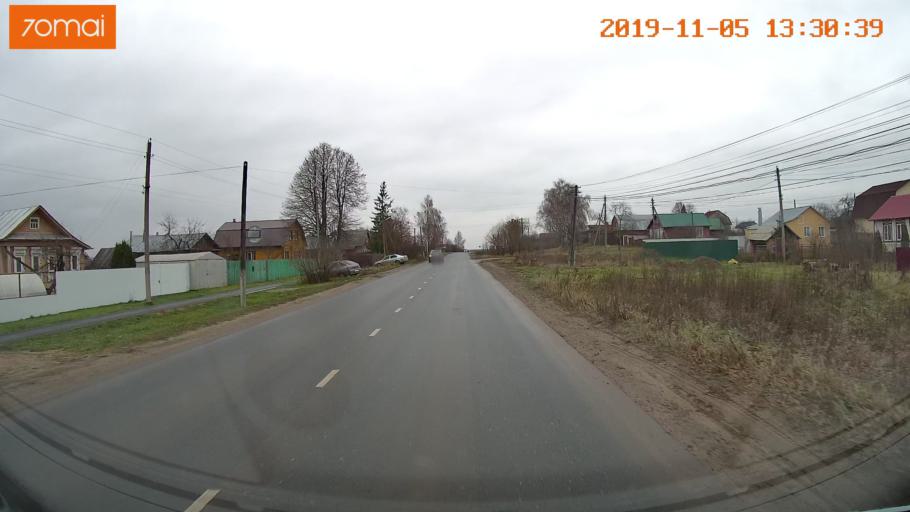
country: RU
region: Ivanovo
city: Shuya
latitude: 56.8685
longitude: 41.3949
